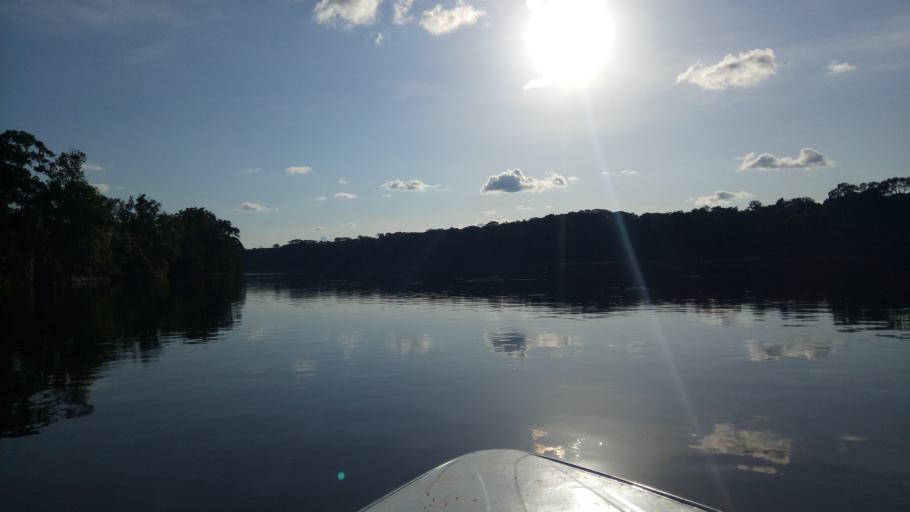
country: CD
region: Eastern Province
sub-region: Sous-Region de la Tshopo
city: Yangambi
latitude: 0.2555
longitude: 24.0567
